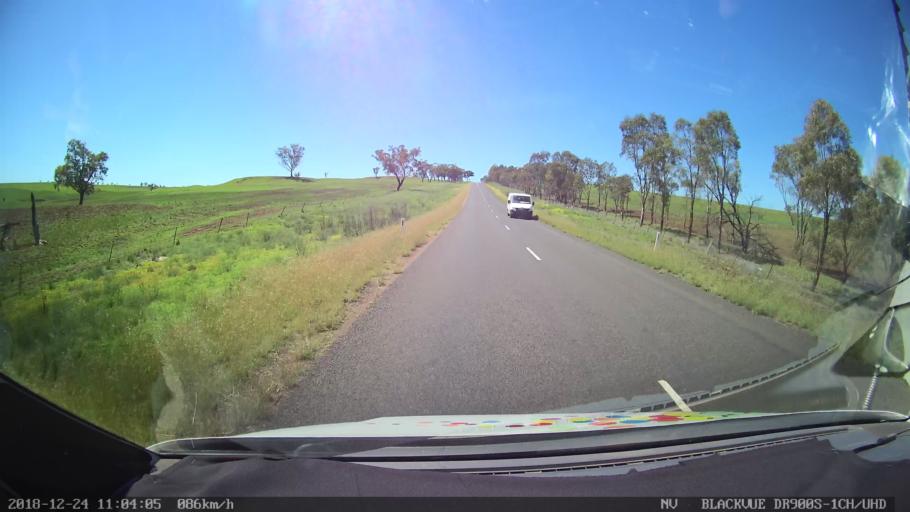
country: AU
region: New South Wales
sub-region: Upper Hunter Shire
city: Merriwa
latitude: -32.1049
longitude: 150.3702
